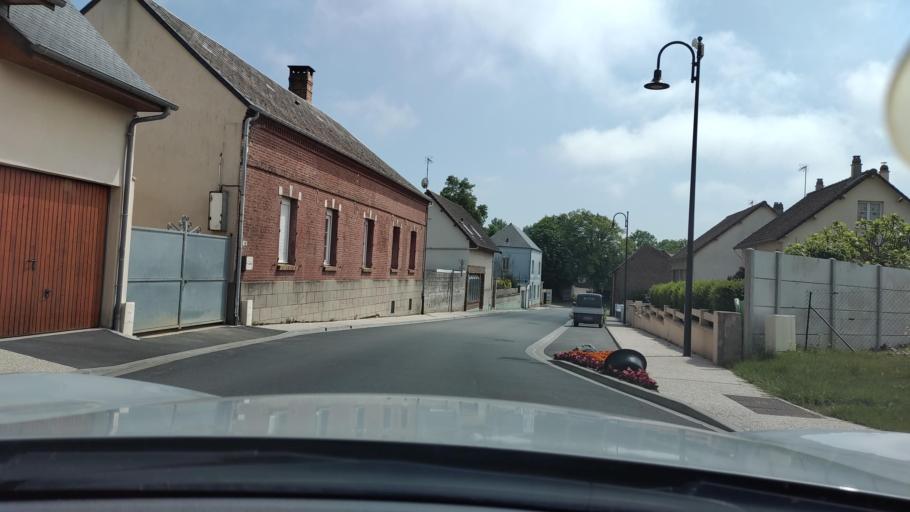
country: FR
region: Picardie
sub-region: Departement de la Somme
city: Ault
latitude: 50.0701
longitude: 1.4603
